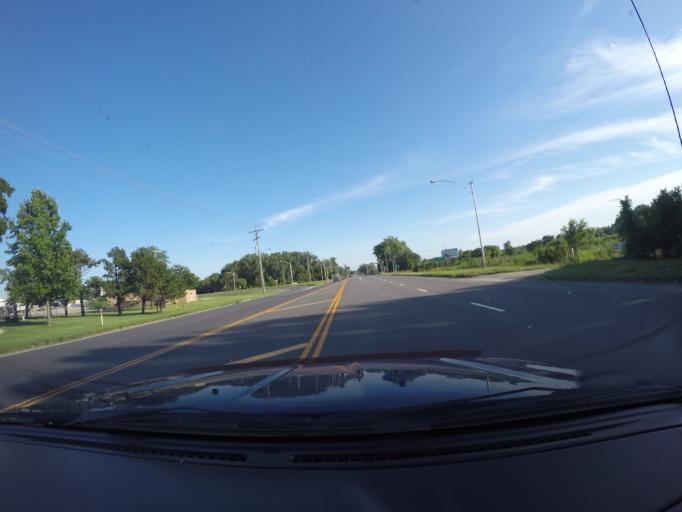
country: US
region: Kansas
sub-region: Douglas County
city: Lawrence
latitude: 39.0019
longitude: -95.2335
